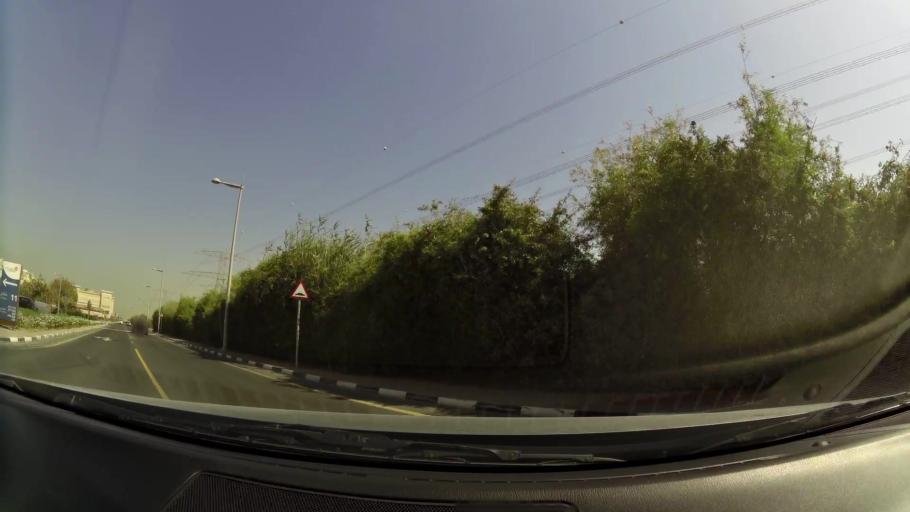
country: AE
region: Dubai
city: Dubai
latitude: 25.0330
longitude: 55.1562
